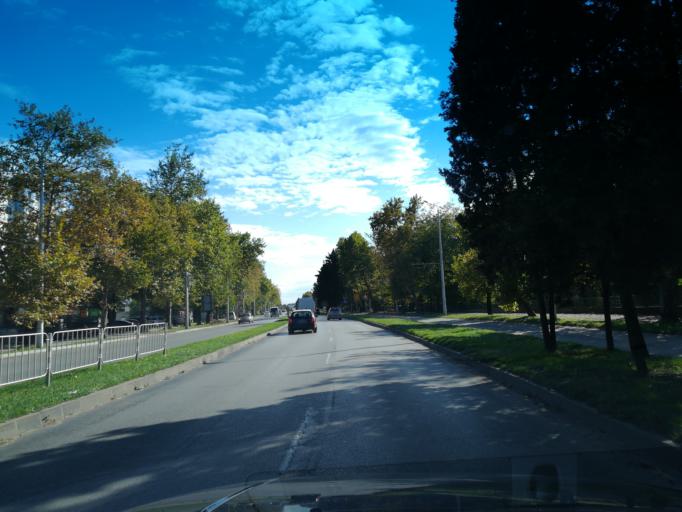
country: BG
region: Stara Zagora
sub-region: Obshtina Stara Zagora
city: Stara Zagora
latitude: 42.4080
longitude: 25.6403
